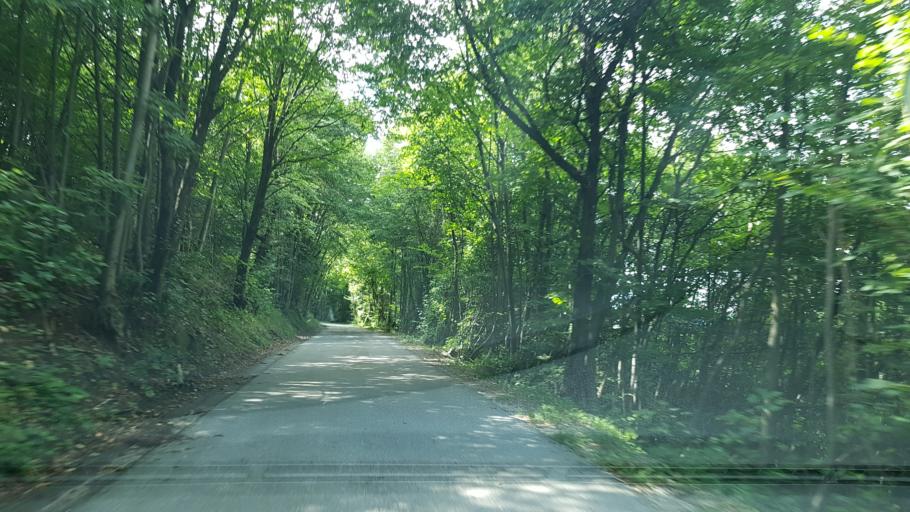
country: SI
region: Kanal
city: Deskle
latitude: 46.0721
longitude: 13.5844
